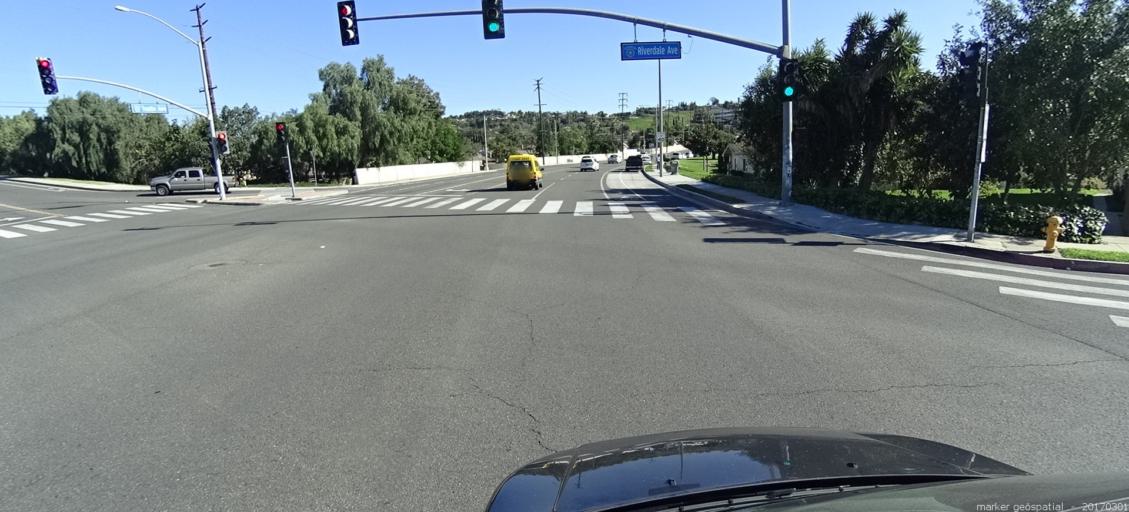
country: US
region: California
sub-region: Orange County
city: Villa Park
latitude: 33.8470
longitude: -117.8350
